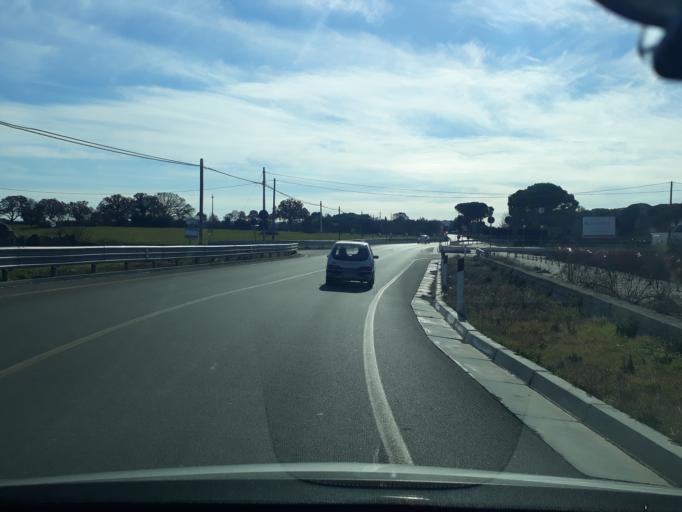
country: IT
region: Apulia
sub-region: Provincia di Bari
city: Locorotondo
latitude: 40.7365
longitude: 17.3326
